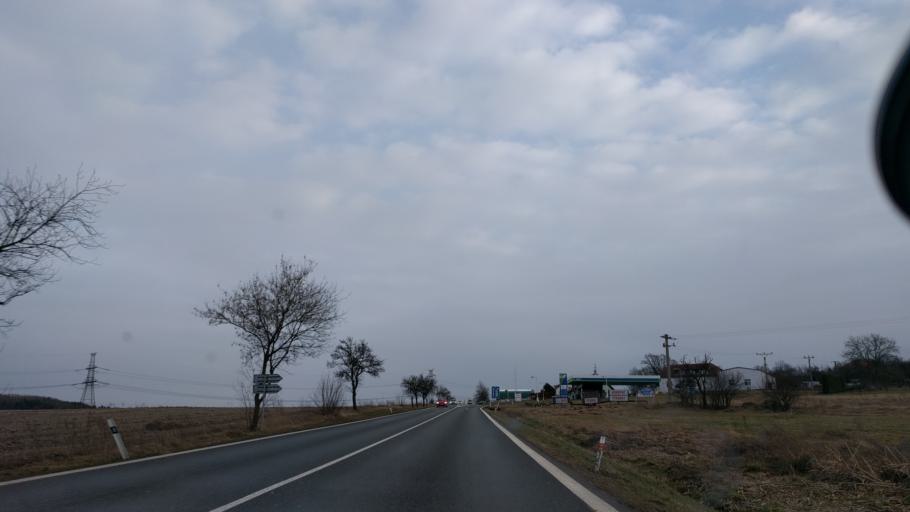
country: CZ
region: Central Bohemia
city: Milin
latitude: 49.5805
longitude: 14.0734
